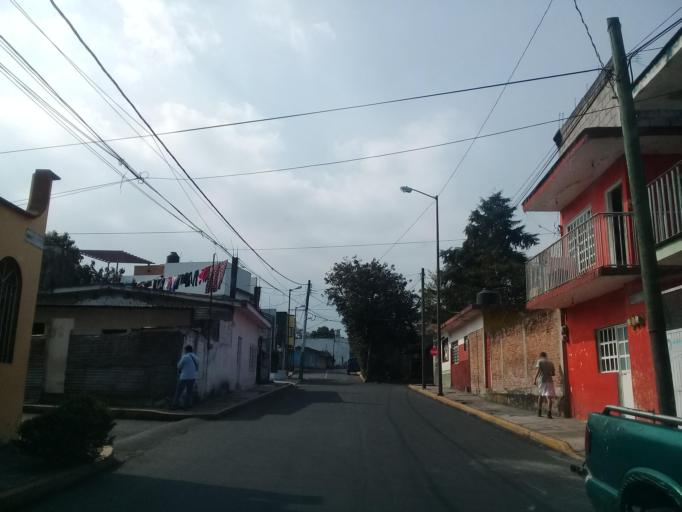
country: MX
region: Veracruz
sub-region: Ixhuatlancillo
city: Union y Progreso
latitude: 18.8675
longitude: -97.1038
